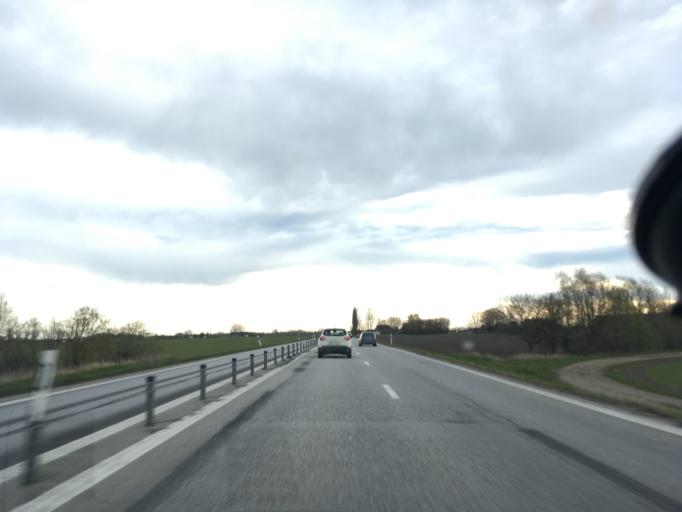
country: SE
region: Skane
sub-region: Vellinge Kommun
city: Vellinge
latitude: 55.4472
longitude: 12.9969
